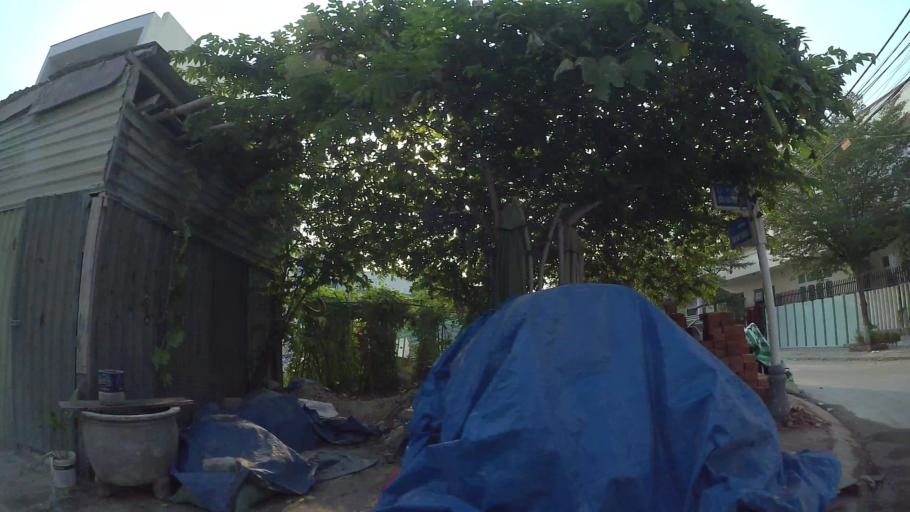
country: VN
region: Da Nang
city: Cam Le
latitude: 16.0163
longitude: 108.1957
